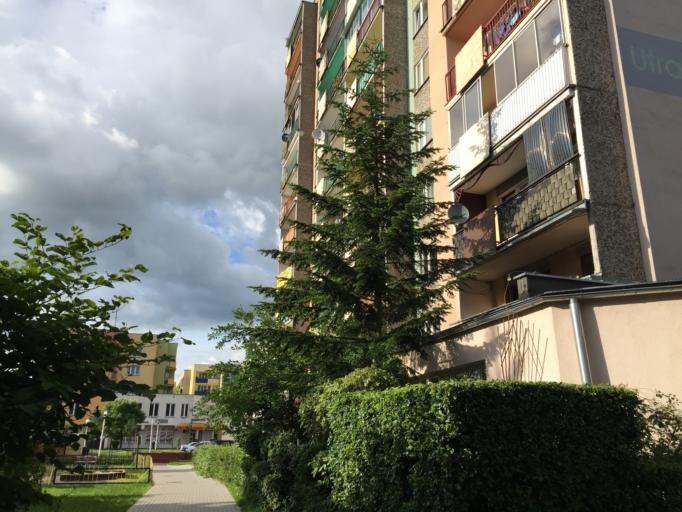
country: PL
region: Podlasie
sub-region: Suwalki
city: Suwalki
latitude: 54.1033
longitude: 22.9366
